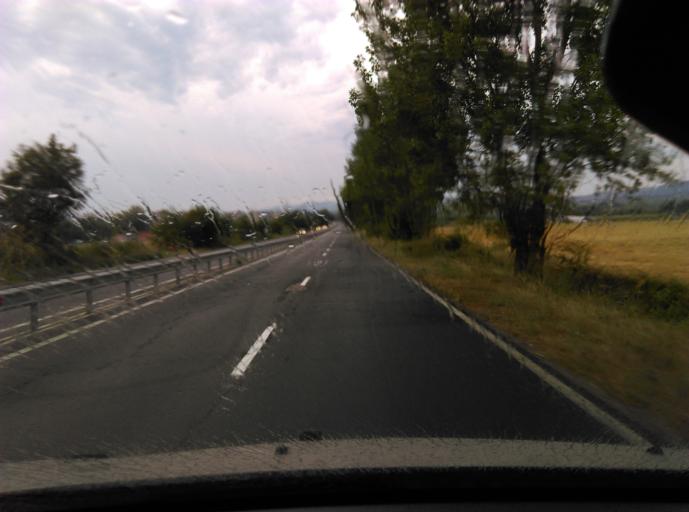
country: BG
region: Burgas
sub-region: Obshtina Sozopol
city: Chernomorets
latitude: 42.4258
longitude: 27.6409
